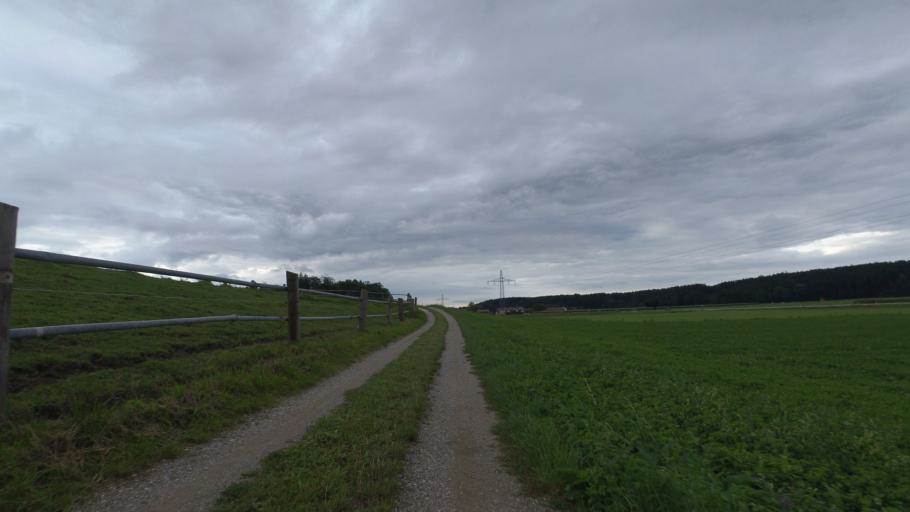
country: DE
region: Bavaria
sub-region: Upper Bavaria
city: Nussdorf
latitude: 47.8818
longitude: 12.5823
